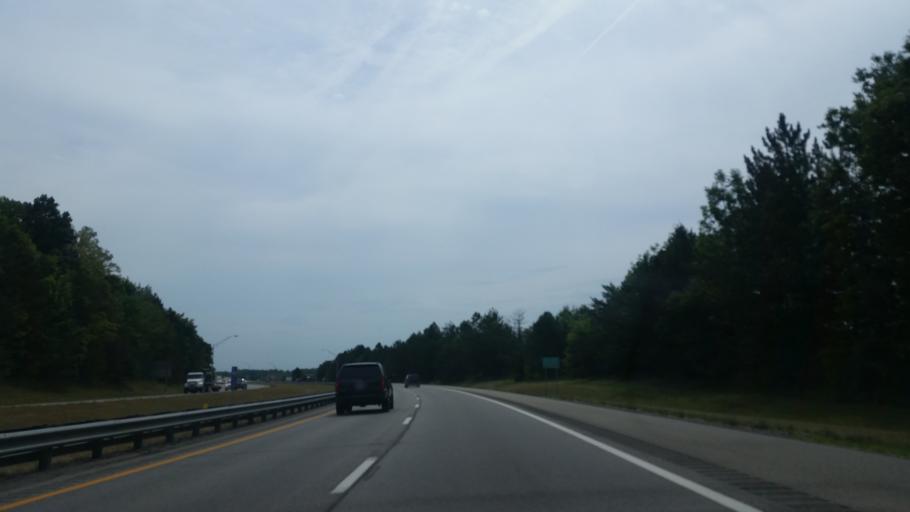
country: US
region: Ohio
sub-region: Cuyahoga County
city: Solon
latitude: 41.3950
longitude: -81.4474
